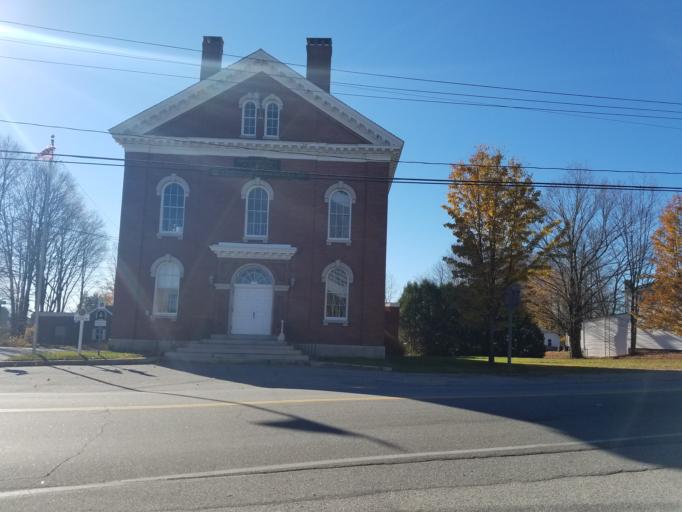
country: US
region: Maine
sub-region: York County
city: Limerick
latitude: 43.6887
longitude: -70.7949
